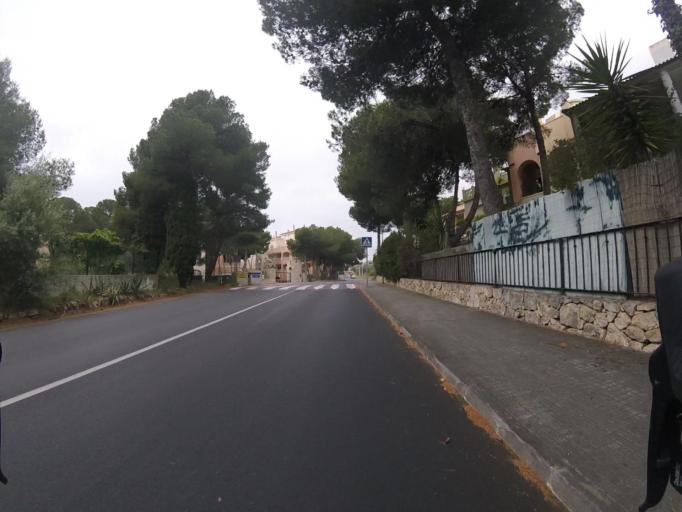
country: ES
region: Valencia
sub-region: Provincia de Castello
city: Peniscola
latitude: 40.3454
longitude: 0.3869
